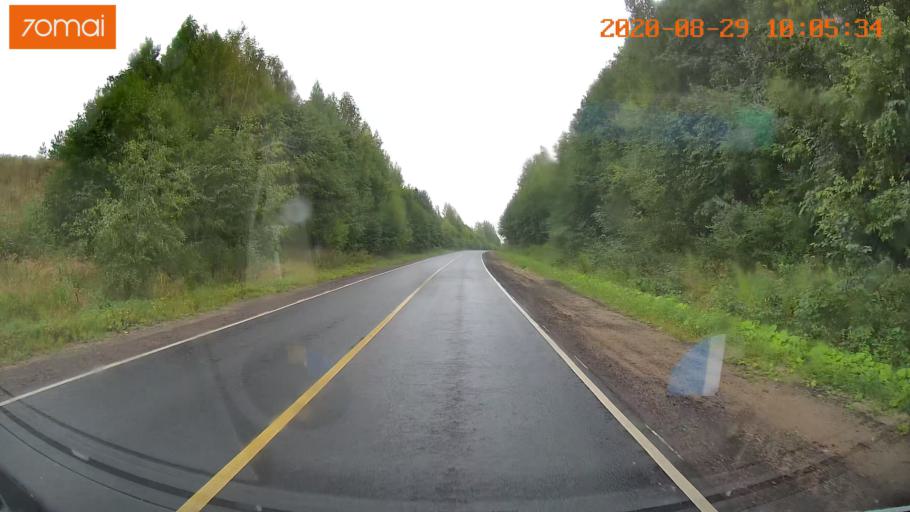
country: RU
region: Ivanovo
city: Zarechnyy
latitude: 57.3925
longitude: 42.5244
